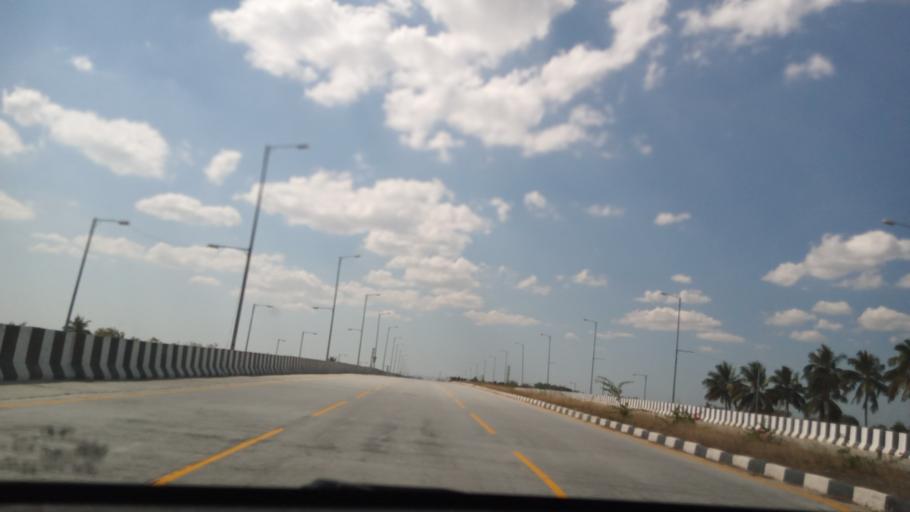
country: IN
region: Andhra Pradesh
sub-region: Chittoor
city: Palmaner
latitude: 13.2117
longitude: 78.7539
